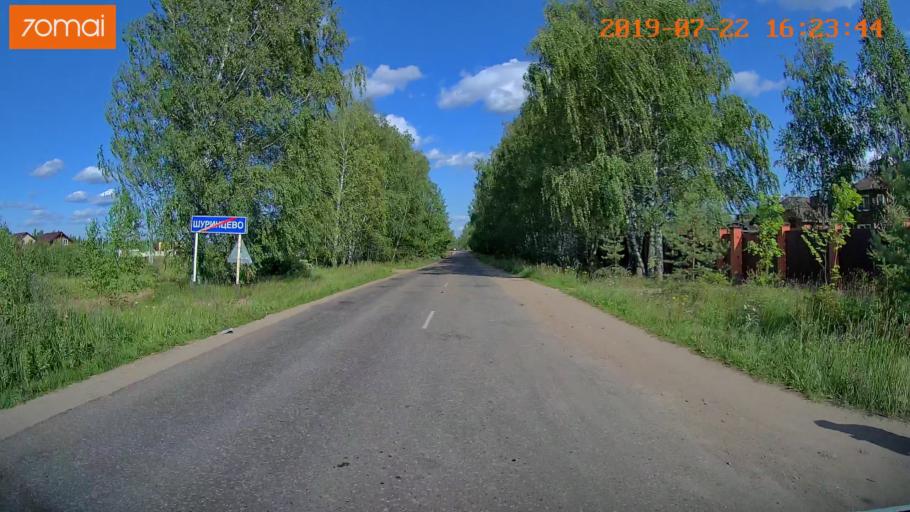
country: RU
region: Ivanovo
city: Novo-Talitsy
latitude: 57.0588
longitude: 40.9024
